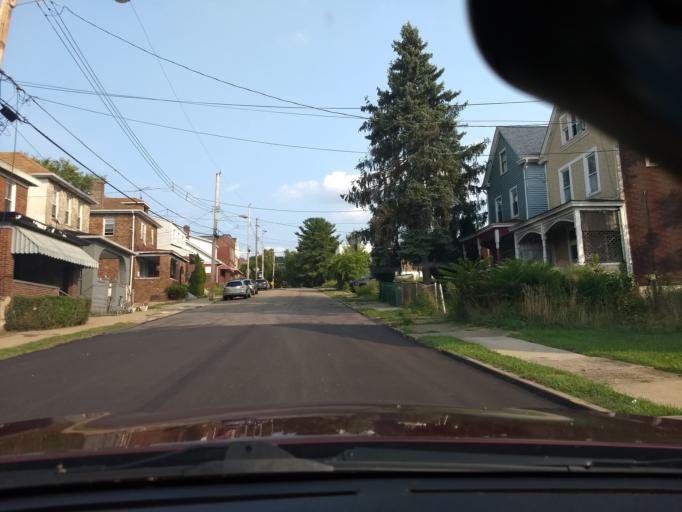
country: US
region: Pennsylvania
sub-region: Allegheny County
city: Aspinwall
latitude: 40.4698
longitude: -79.9067
